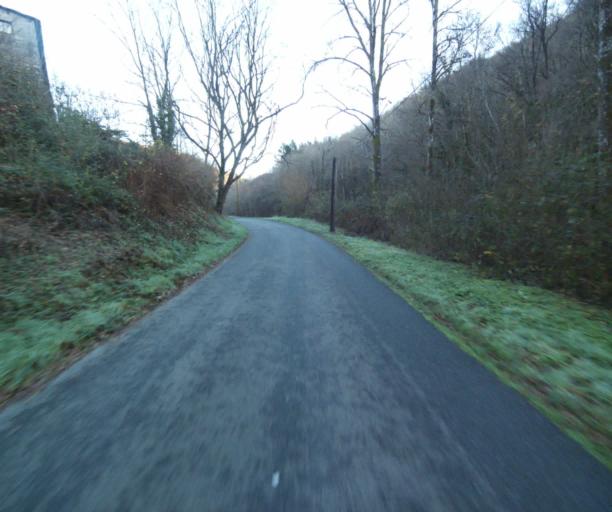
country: FR
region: Limousin
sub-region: Departement de la Correze
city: Laguenne
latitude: 45.2401
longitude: 1.7909
